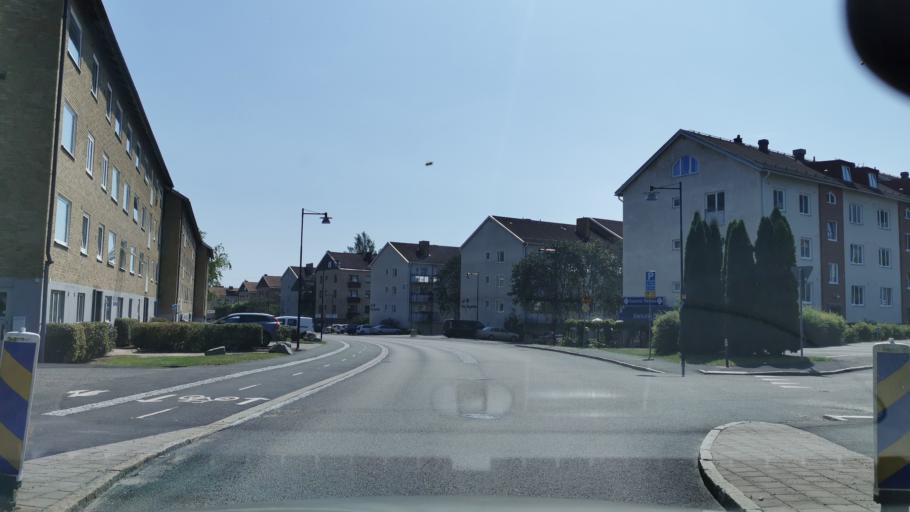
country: SE
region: Vaestra Goetaland
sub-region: Molndal
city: Moelndal
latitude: 57.6773
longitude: 11.9892
